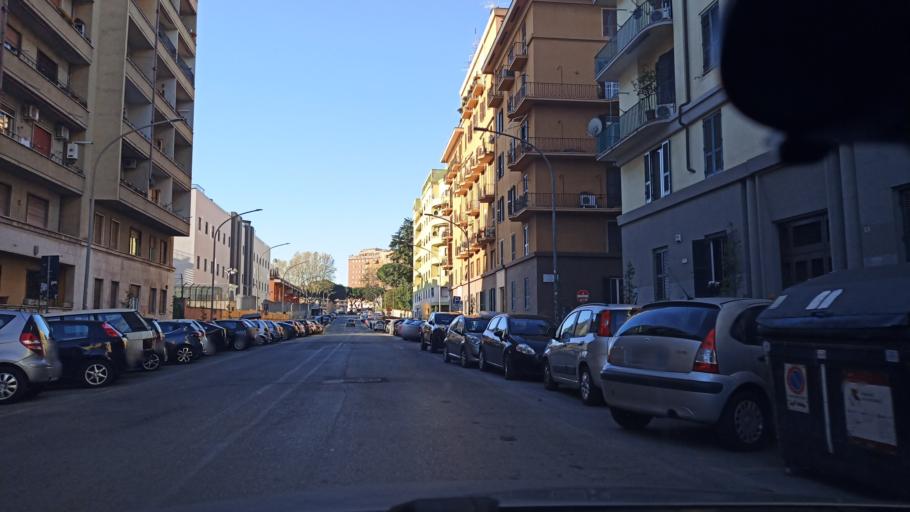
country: IT
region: Latium
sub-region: Citta metropolitana di Roma Capitale
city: Rome
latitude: 41.8792
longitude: 12.5111
